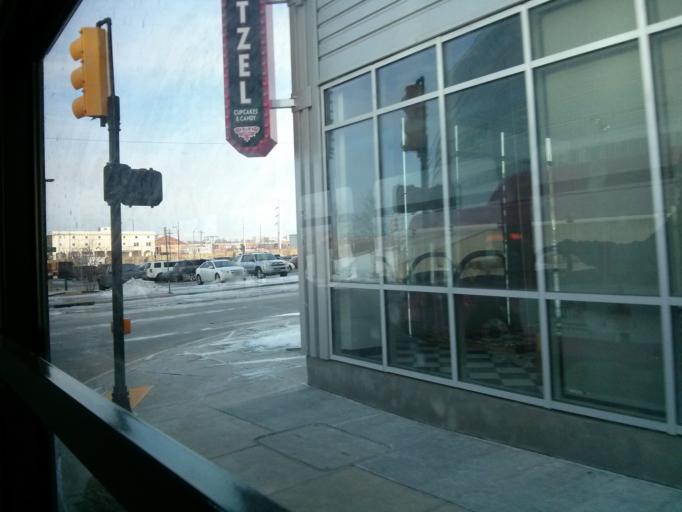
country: US
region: Oklahoma
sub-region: Tulsa County
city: Tulsa
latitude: 36.1530
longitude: -95.9951
